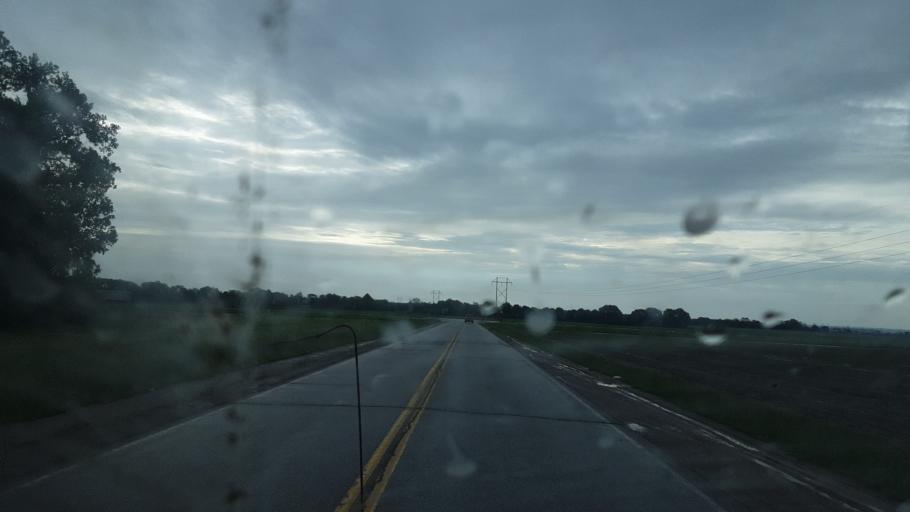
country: US
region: Missouri
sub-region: Clark County
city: Kahoka
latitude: 40.4307
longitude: -91.5735
